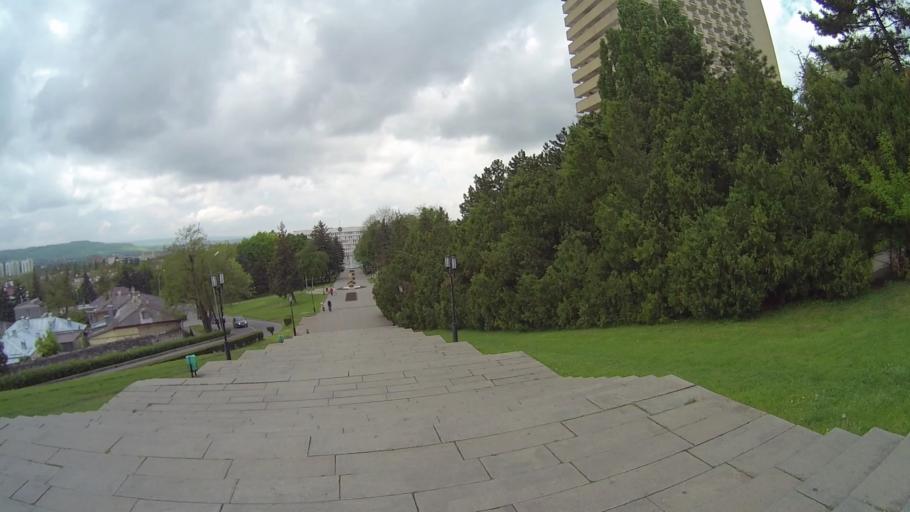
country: RU
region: Stavropol'skiy
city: Pyatigorsk
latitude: 44.0402
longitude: 43.0748
